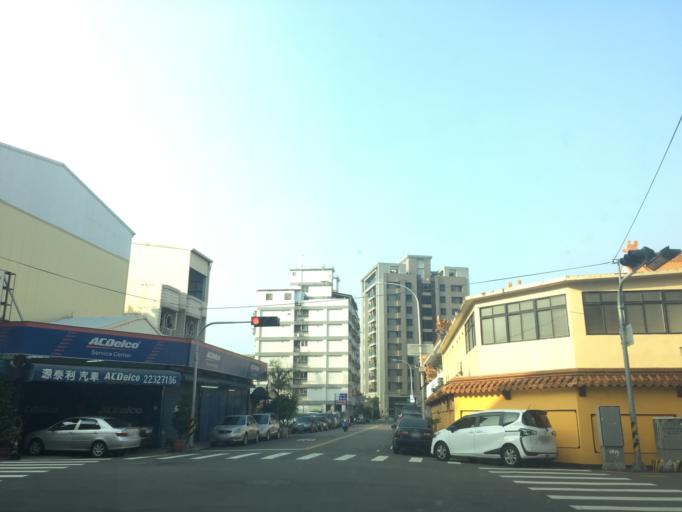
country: TW
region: Taiwan
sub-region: Taichung City
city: Taichung
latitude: 24.1689
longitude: 120.6907
